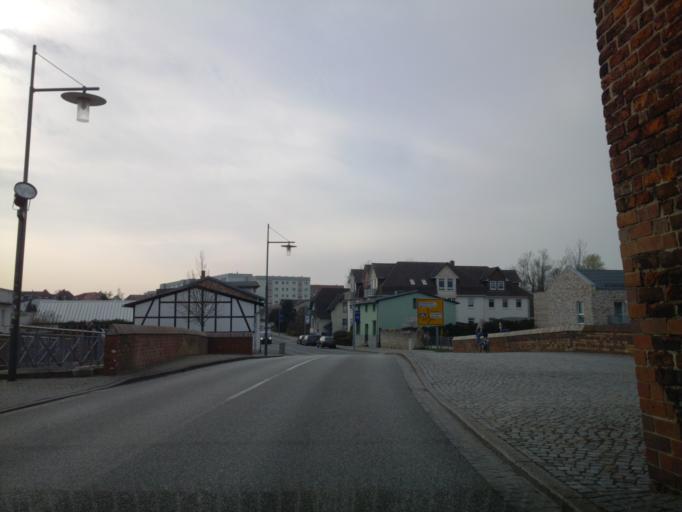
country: DE
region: Mecklenburg-Vorpommern
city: Ribnitz-Damgarten
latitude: 54.2436
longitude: 12.4264
